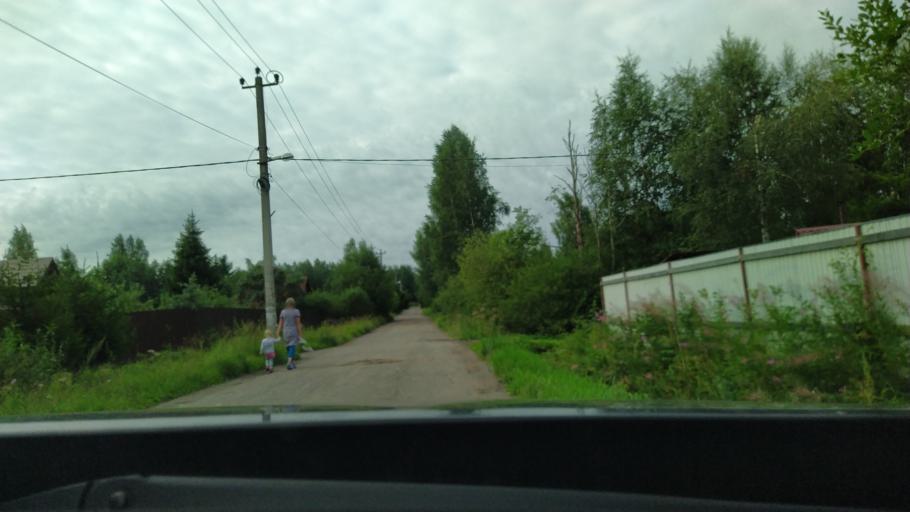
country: RU
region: Leningrad
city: Otradnoye
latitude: 59.7304
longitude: 30.8472
